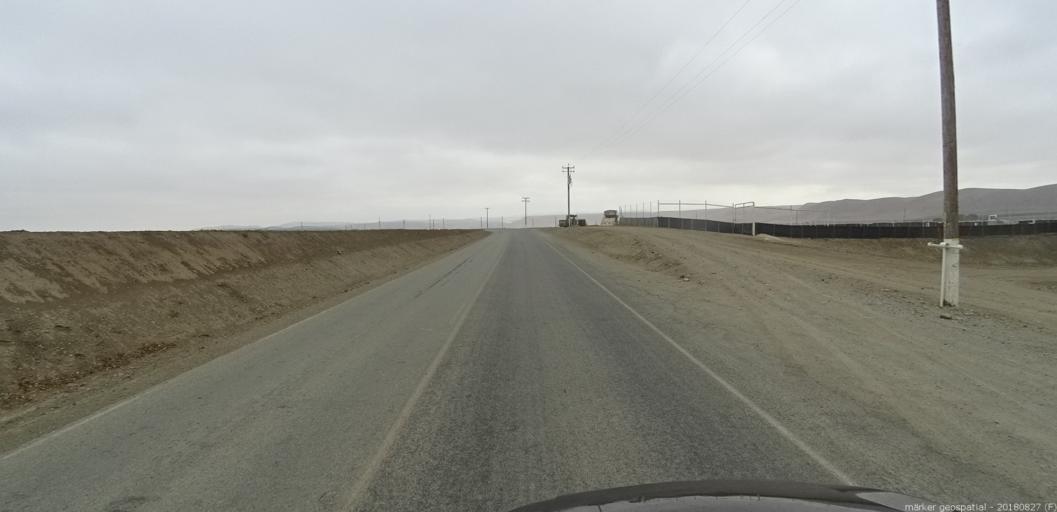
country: US
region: California
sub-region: Monterey County
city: King City
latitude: 36.2302
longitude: -121.1074
